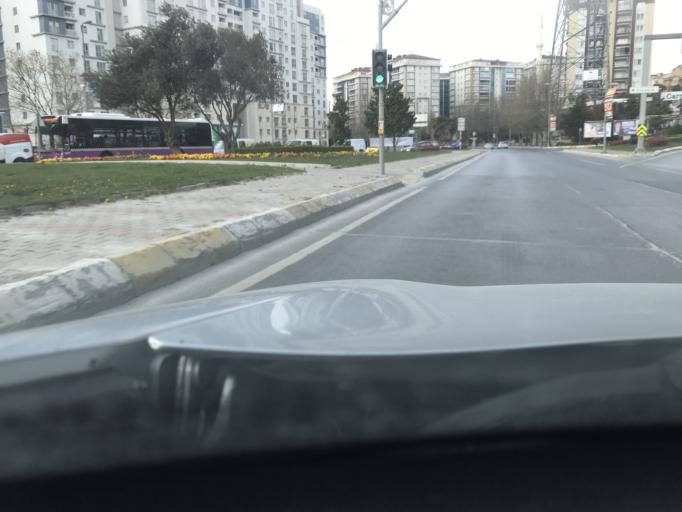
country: TR
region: Istanbul
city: Esenyurt
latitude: 41.0562
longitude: 28.6713
